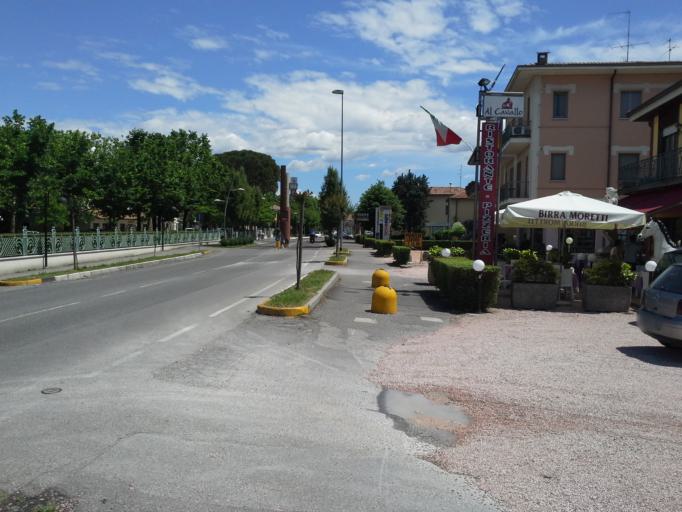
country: IT
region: Lombardy
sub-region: Provincia di Brescia
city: San Martino della Battaglia
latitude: 45.4619
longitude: 10.6203
